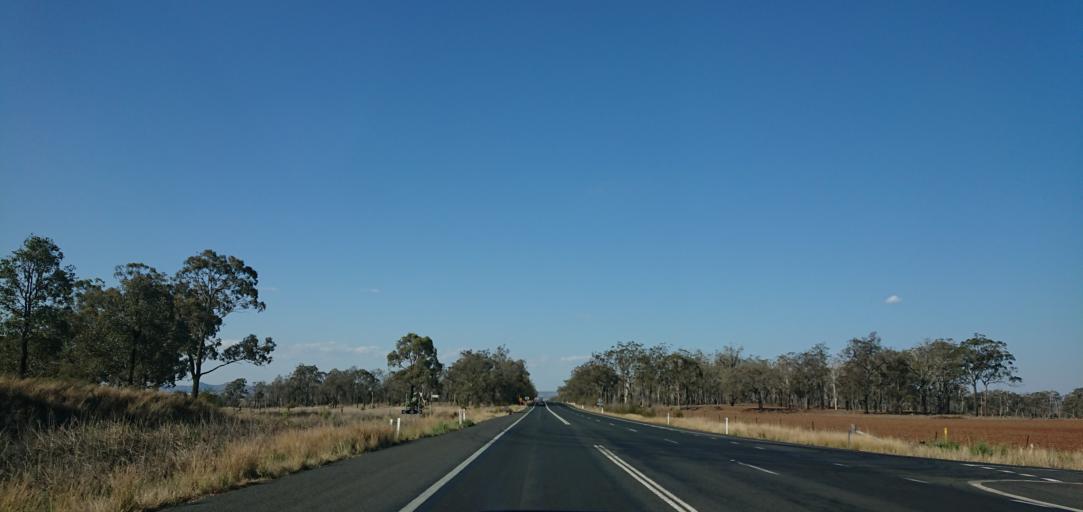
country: AU
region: Queensland
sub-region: Toowoomba
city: Westbrook
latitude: -27.6251
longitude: 151.7604
